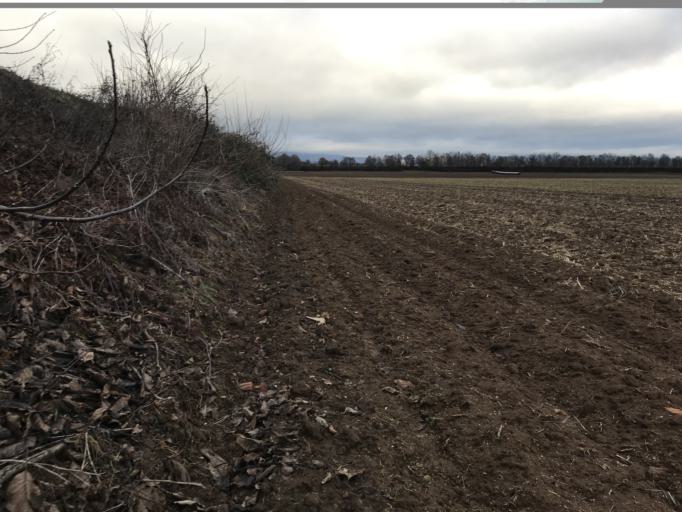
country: DE
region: Rheinland-Pfalz
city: Klein-Winternheim
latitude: 49.9853
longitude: 8.2102
